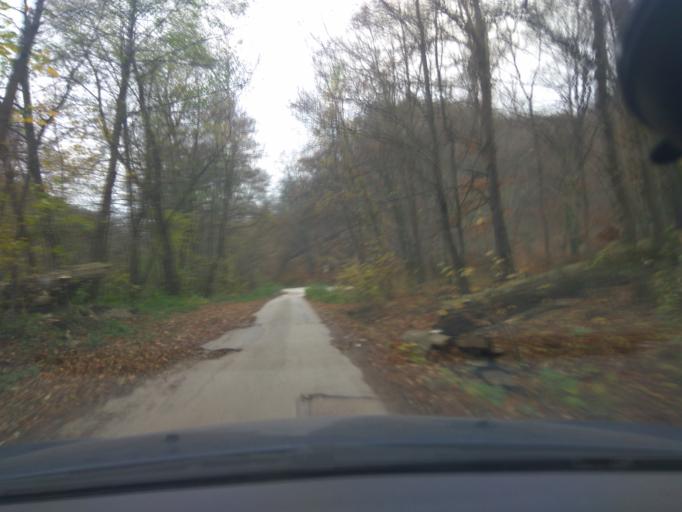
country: SK
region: Trnavsky
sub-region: Okres Trnava
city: Piestany
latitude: 48.6076
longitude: 17.9260
